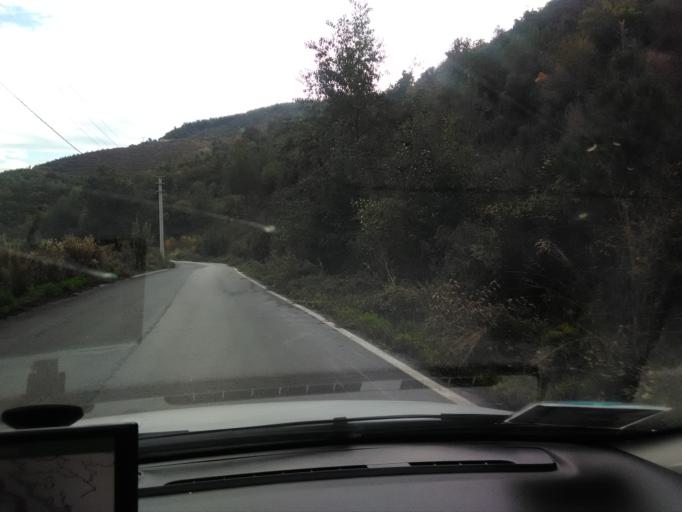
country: TR
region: Antalya
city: Gazipasa
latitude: 36.2632
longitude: 32.3782
